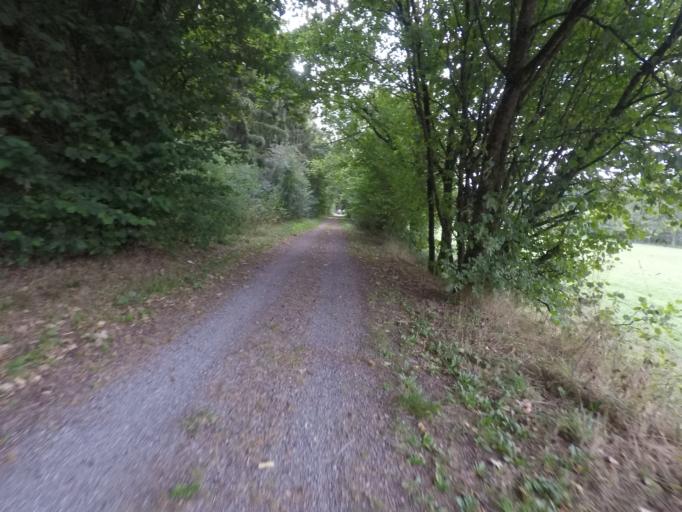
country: BE
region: Wallonia
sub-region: Province du Luxembourg
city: Martelange
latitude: 49.8460
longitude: 5.7111
